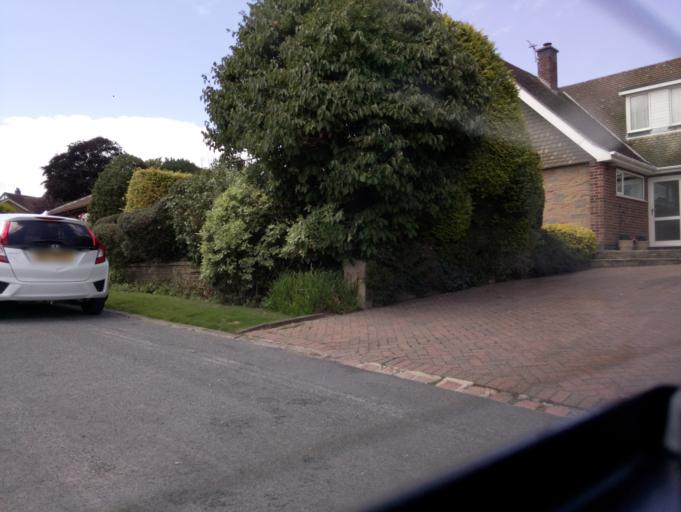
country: GB
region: England
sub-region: Nottinghamshire
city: Cotgrave
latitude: 52.8816
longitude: -1.0852
